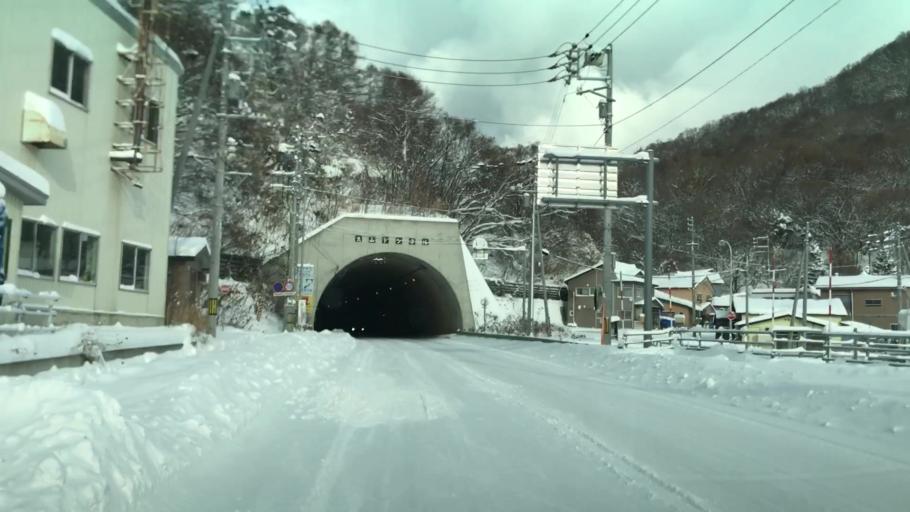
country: JP
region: Hokkaido
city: Yoichi
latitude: 43.2805
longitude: 140.6377
